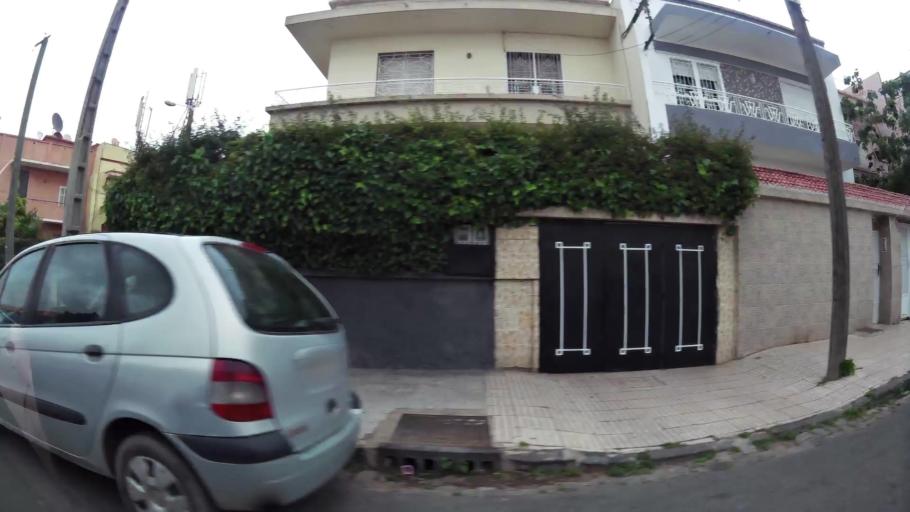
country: MA
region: Grand Casablanca
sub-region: Casablanca
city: Casablanca
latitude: 33.5684
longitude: -7.6176
